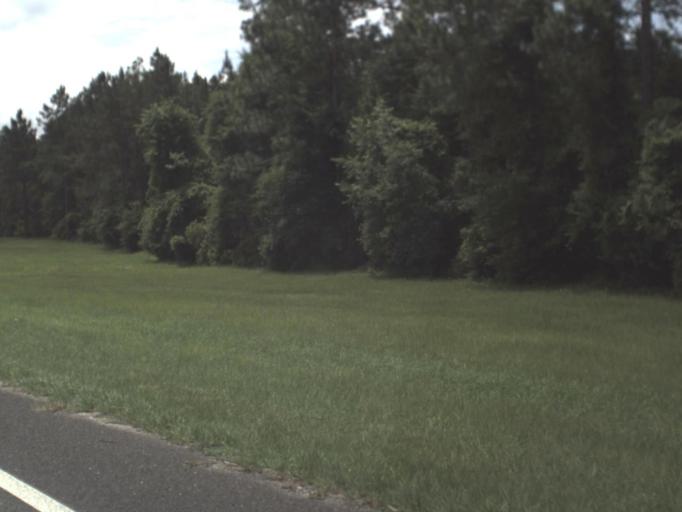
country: US
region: Georgia
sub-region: Charlton County
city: Folkston
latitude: 30.7691
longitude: -81.9731
